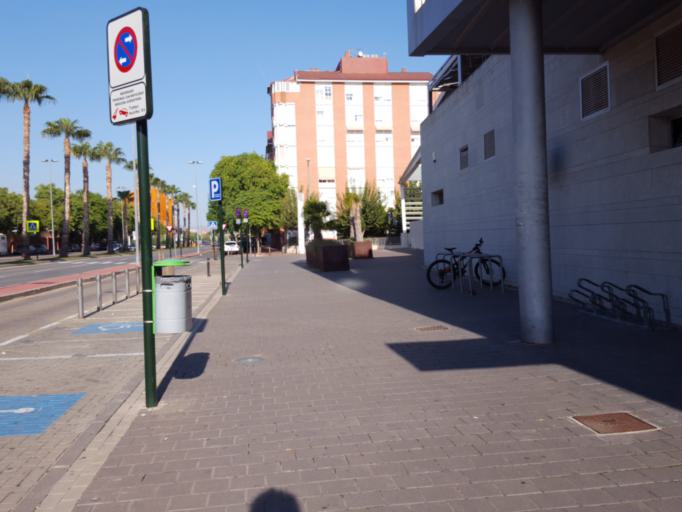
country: ES
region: Murcia
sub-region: Murcia
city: Murcia
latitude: 37.9949
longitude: -1.1215
